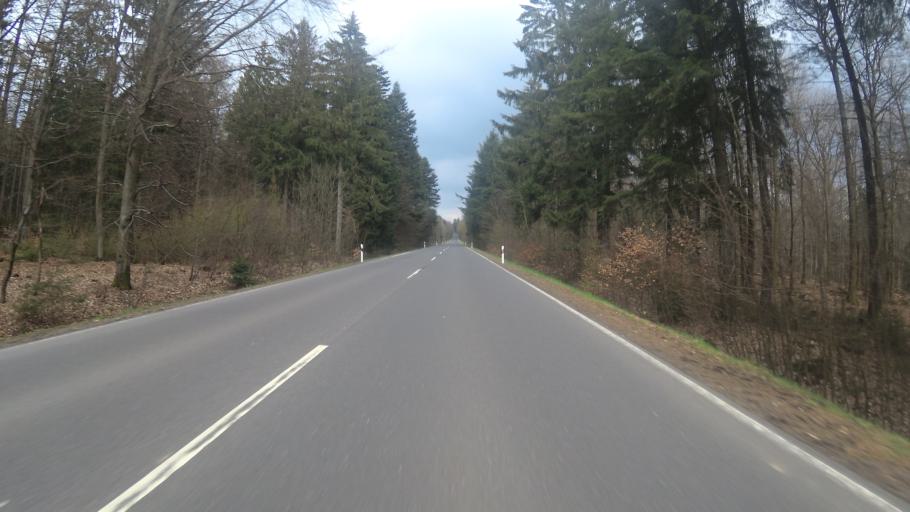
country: DE
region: Saarland
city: Nonnweiler
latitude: 49.6343
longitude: 6.9532
